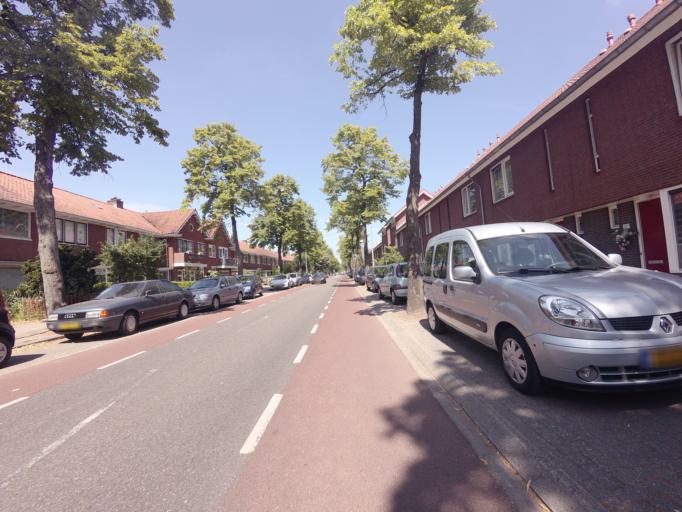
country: NL
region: Utrecht
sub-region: Gemeente Utrecht
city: Lunetten
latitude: 52.0620
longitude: 5.1178
